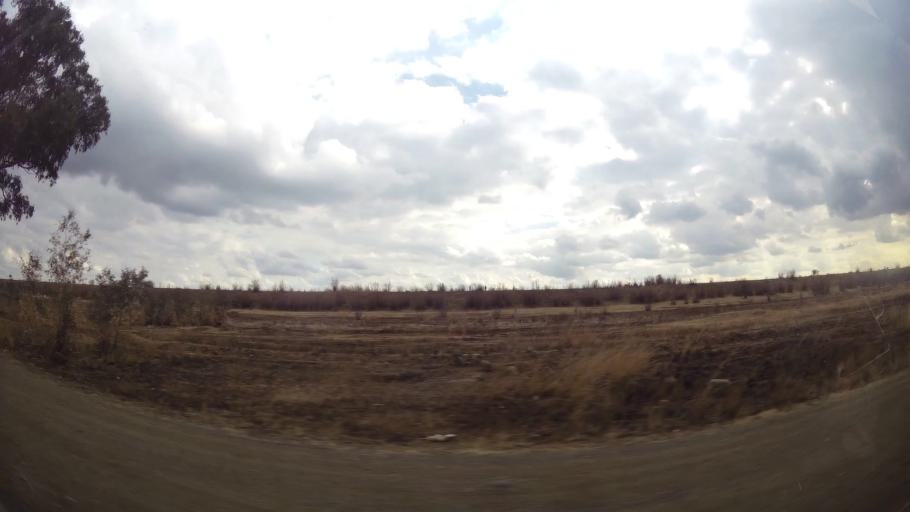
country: ZA
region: Orange Free State
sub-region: Fezile Dabi District Municipality
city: Sasolburg
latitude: -26.8759
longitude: 27.8869
